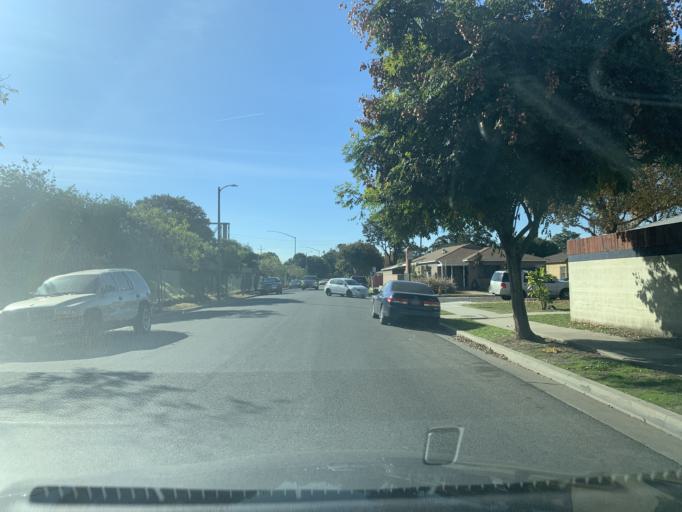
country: US
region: California
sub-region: Los Angeles County
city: East Rancho Dominguez
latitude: 33.8667
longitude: -118.1973
